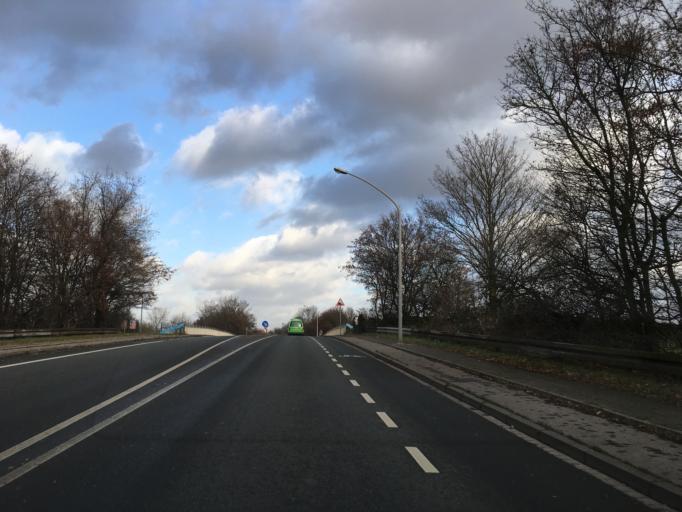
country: DE
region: North Rhine-Westphalia
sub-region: Regierungsbezirk Dusseldorf
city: Oberhausen
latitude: 51.5041
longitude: 6.8341
